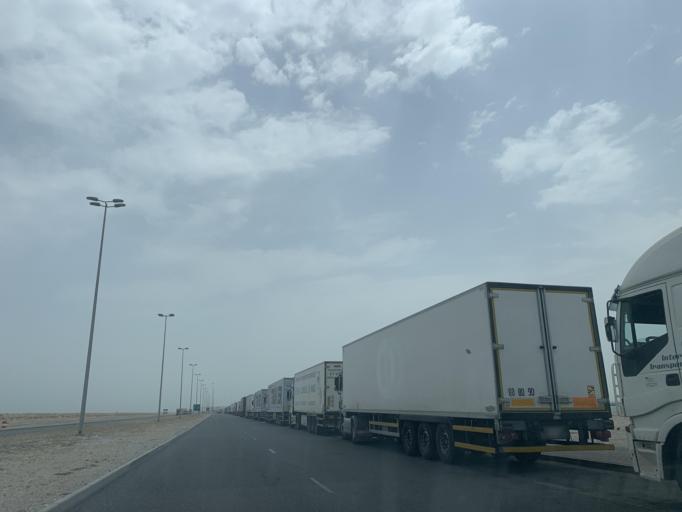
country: BH
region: Muharraq
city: Al Hadd
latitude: 26.2030
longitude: 50.7084
